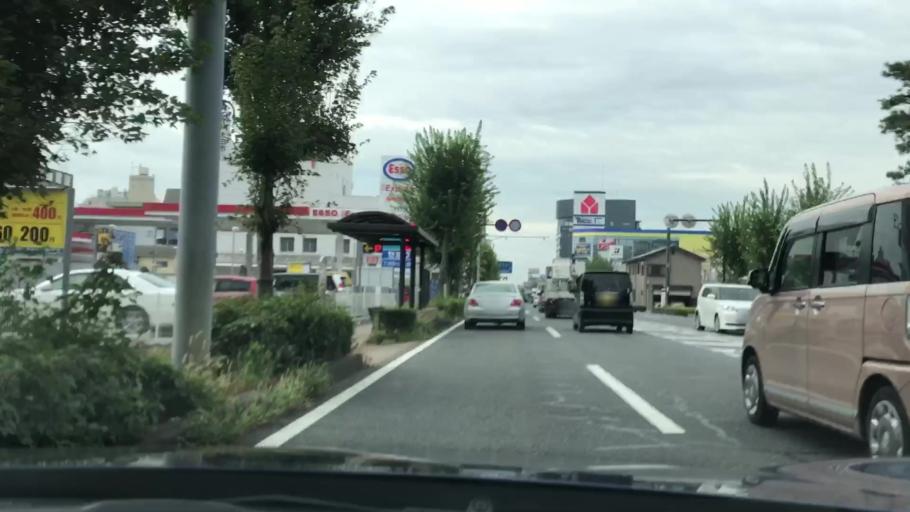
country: JP
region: Gunma
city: Ota
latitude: 36.2911
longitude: 139.3766
